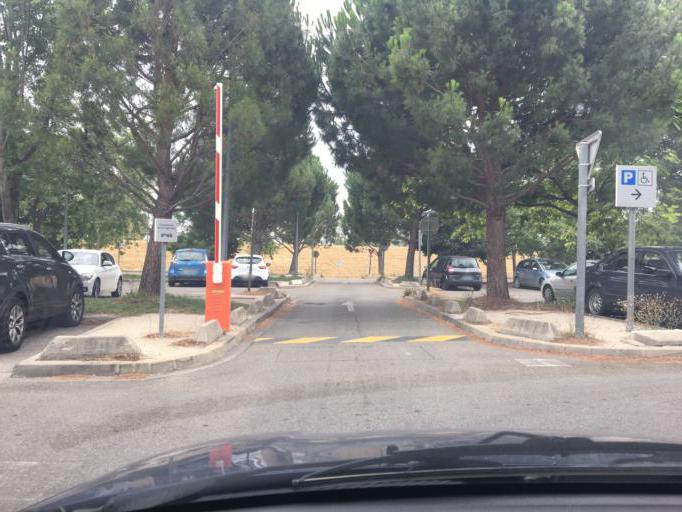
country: FR
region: Provence-Alpes-Cote d'Azur
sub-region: Departement des Bouches-du-Rhone
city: Rognonas
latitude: 43.9180
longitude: 4.8043
